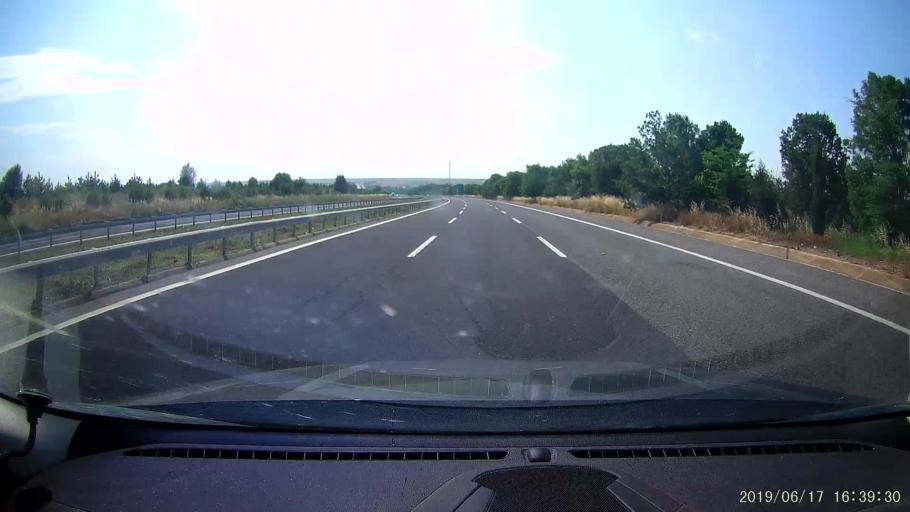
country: TR
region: Kirklareli
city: Luleburgaz
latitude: 41.4495
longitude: 27.4089
